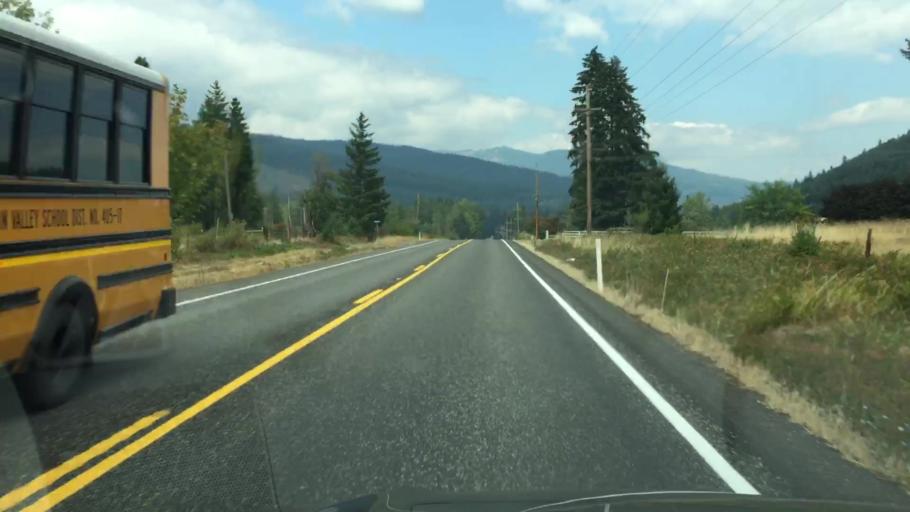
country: US
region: Washington
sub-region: Klickitat County
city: White Salmon
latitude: 45.8403
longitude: -121.5018
